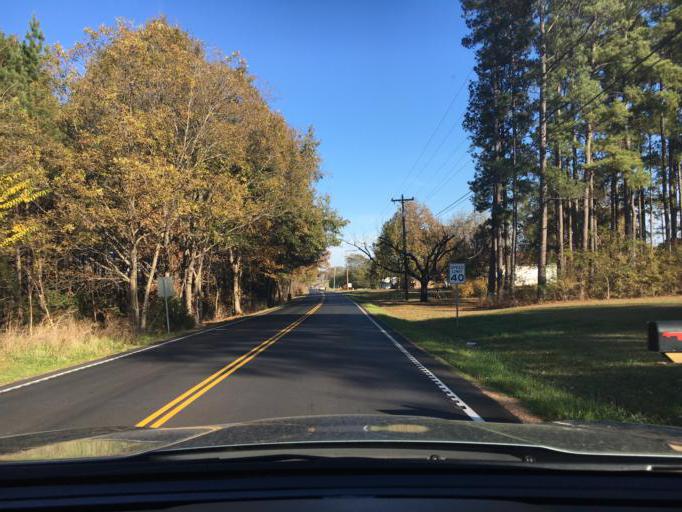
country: US
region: South Carolina
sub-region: Spartanburg County
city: Inman Mills
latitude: 35.0299
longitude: -82.1144
